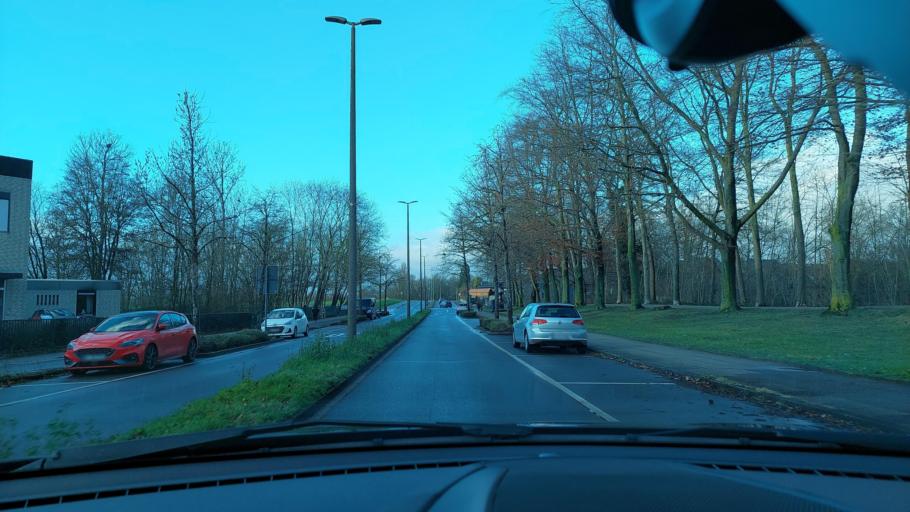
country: DE
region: North Rhine-Westphalia
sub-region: Regierungsbezirk Dusseldorf
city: Dormagen
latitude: 51.0641
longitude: 6.8085
